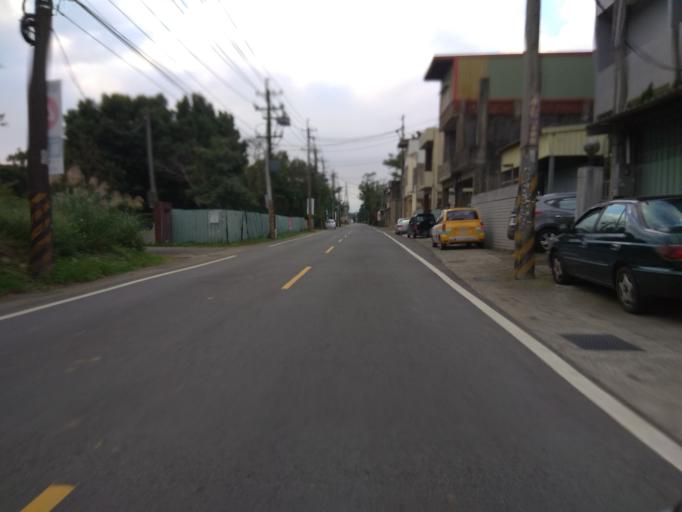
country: TW
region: Taiwan
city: Daxi
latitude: 24.8393
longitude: 121.2069
